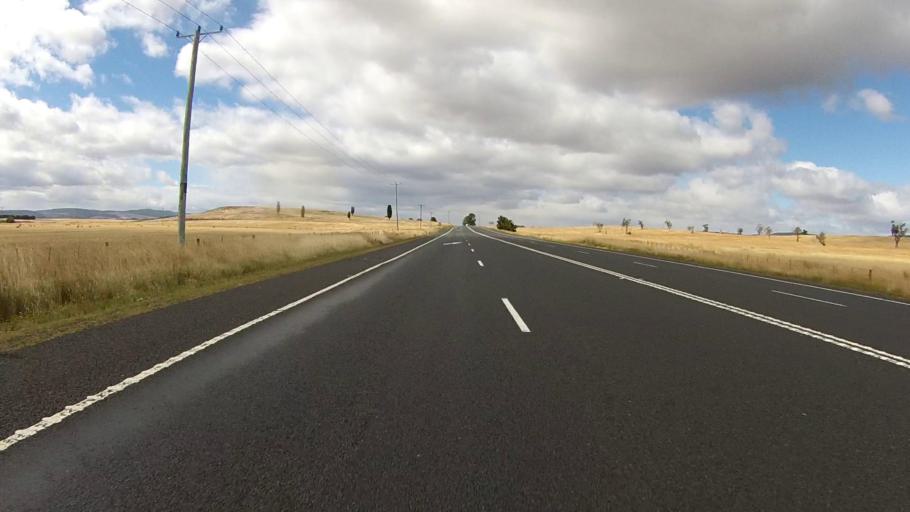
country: AU
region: Tasmania
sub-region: Northern Midlands
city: Evandale
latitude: -41.8740
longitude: 147.4612
